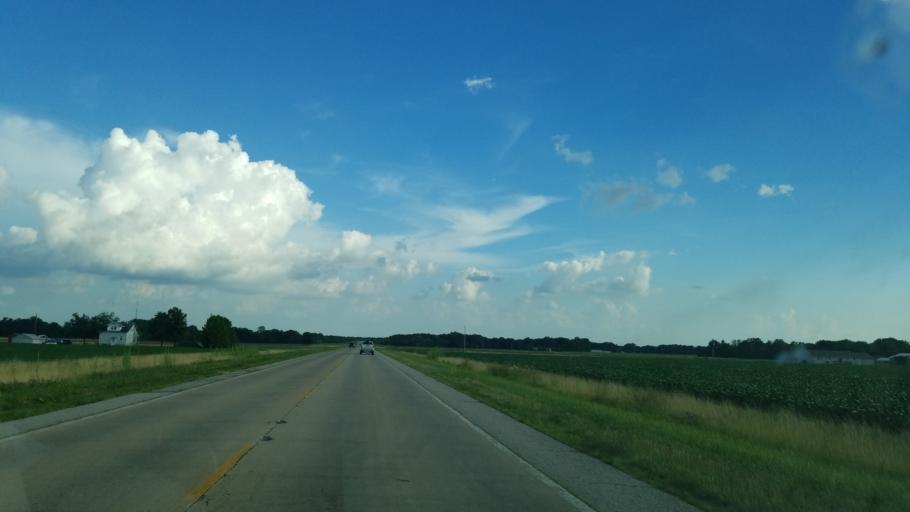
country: US
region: Illinois
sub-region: Marion County
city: Sandoval
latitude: 38.5931
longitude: -89.1084
